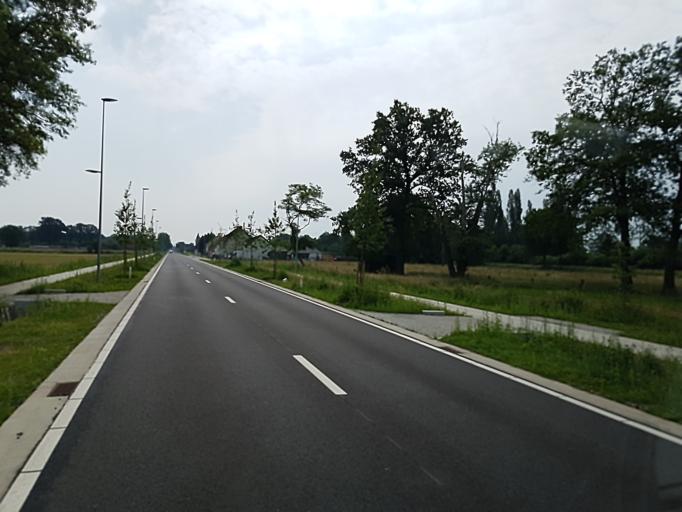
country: BE
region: Flanders
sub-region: Provincie Limburg
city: Leopoldsburg
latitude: 51.1374
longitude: 5.2331
